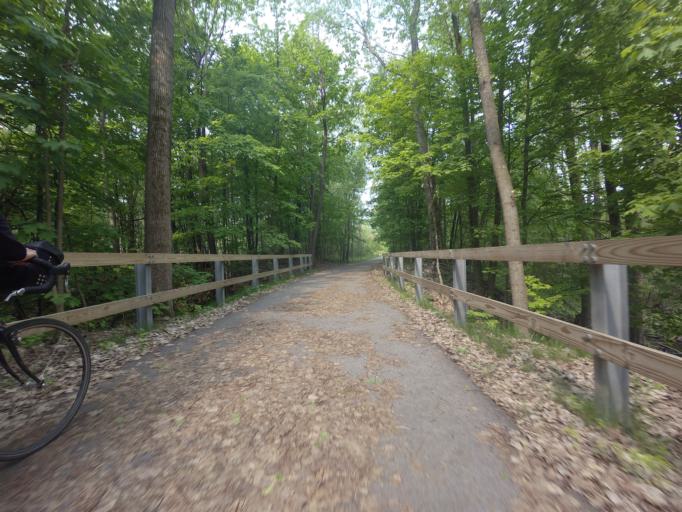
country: US
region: New York
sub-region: Jefferson County
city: Watertown
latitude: 43.9715
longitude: -75.8701
